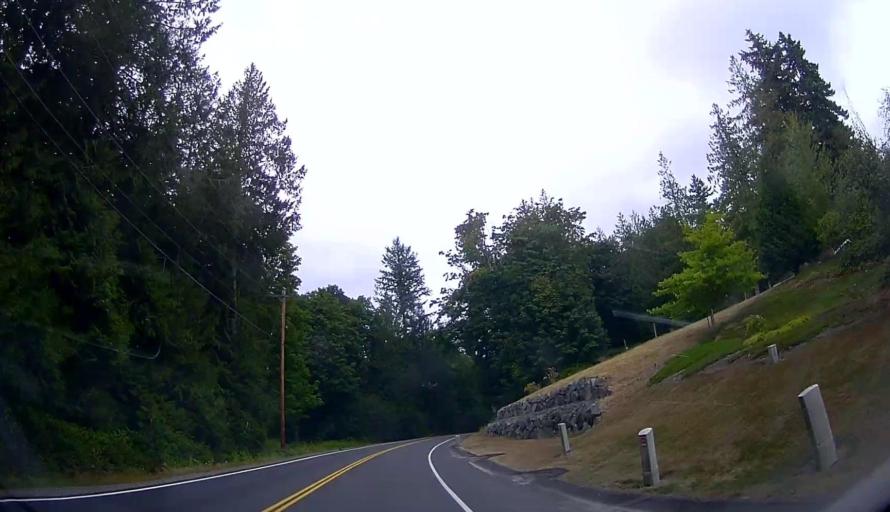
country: US
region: Washington
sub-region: Snohomish County
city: Warm Beach
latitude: 48.1859
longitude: -122.3448
